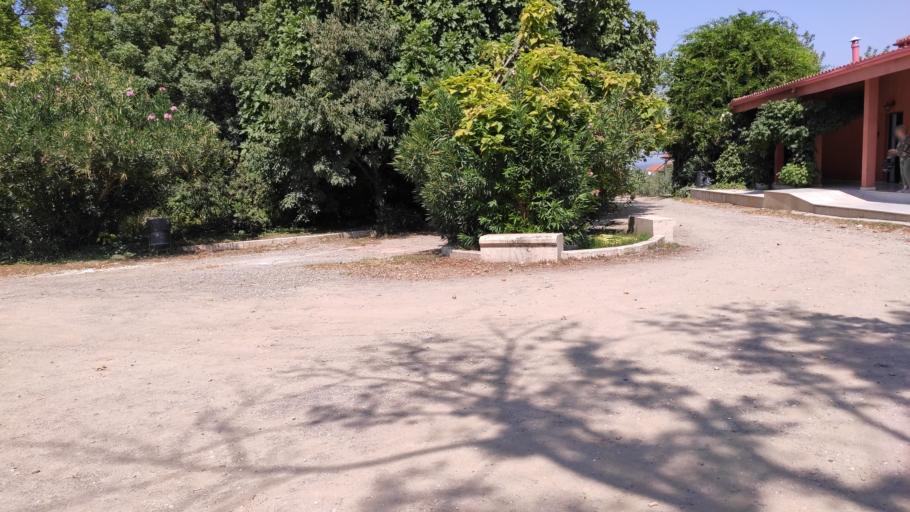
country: GR
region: Central Macedonia
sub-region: Nomos Imathias
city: Vergina
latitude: 40.4879
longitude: 22.3200
